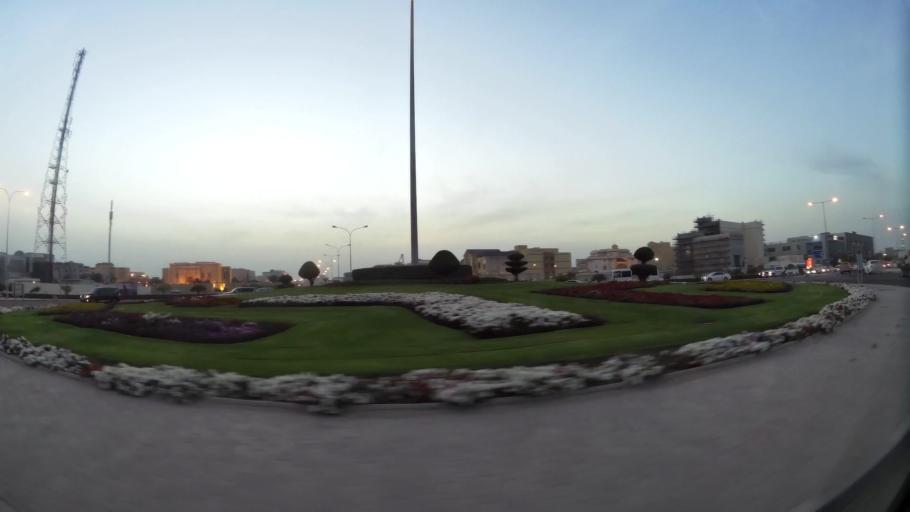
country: QA
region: Al Wakrah
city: Al Wakrah
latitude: 25.1616
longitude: 51.6078
